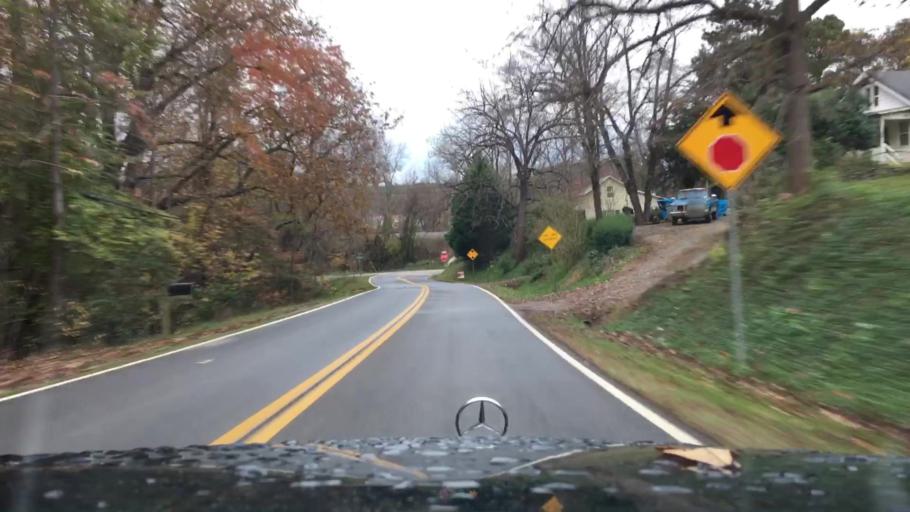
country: US
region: Virginia
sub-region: Pittsylvania County
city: Hurt
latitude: 37.1001
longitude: -79.2995
